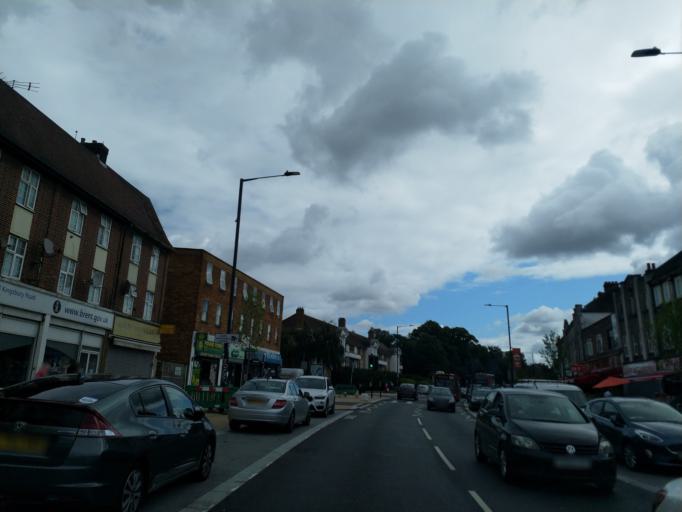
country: GB
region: England
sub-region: Greater London
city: Edgware
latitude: 51.5858
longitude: -0.2768
